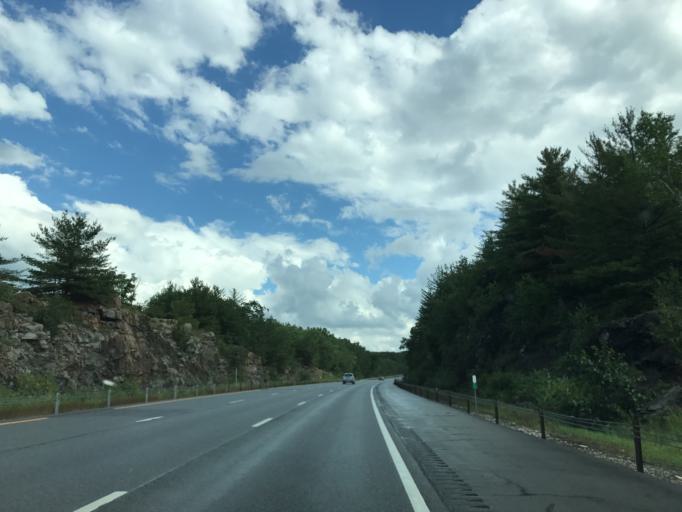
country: US
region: New York
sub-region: Warren County
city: Glens Falls North
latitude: 43.4058
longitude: -73.7162
